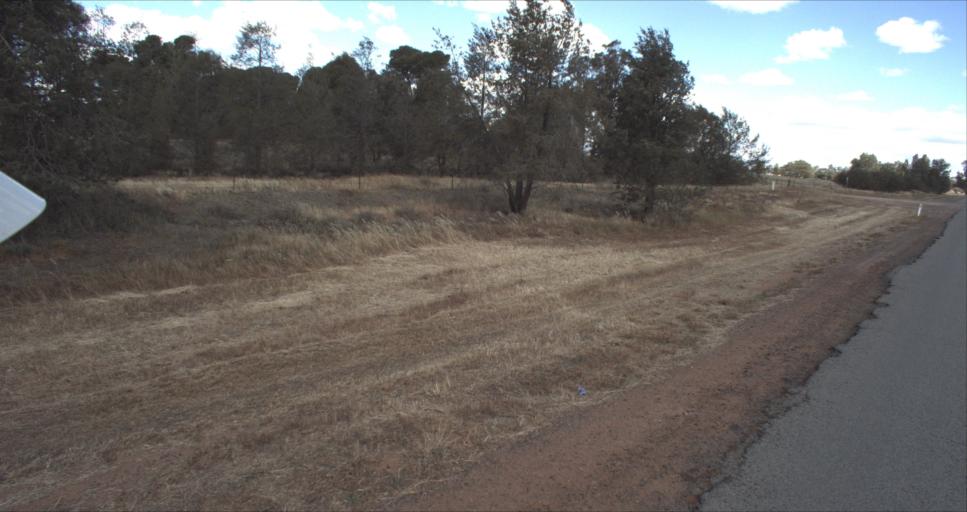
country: AU
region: New South Wales
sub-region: Leeton
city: Leeton
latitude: -34.4817
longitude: 146.2490
